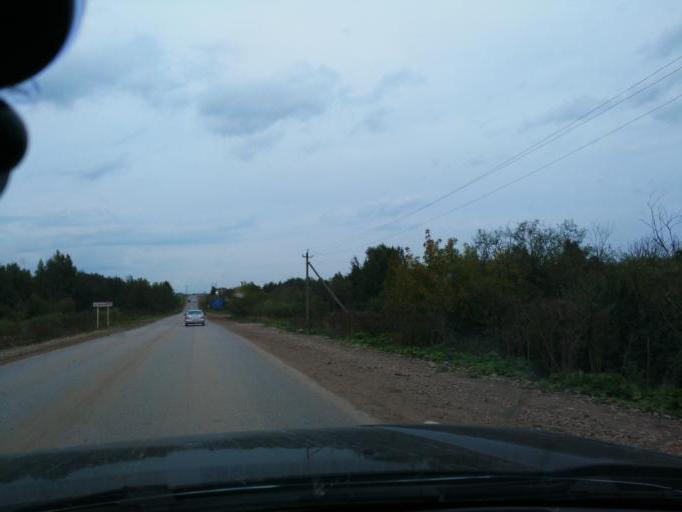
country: RU
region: Perm
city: Chernushka
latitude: 56.5401
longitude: 56.1002
